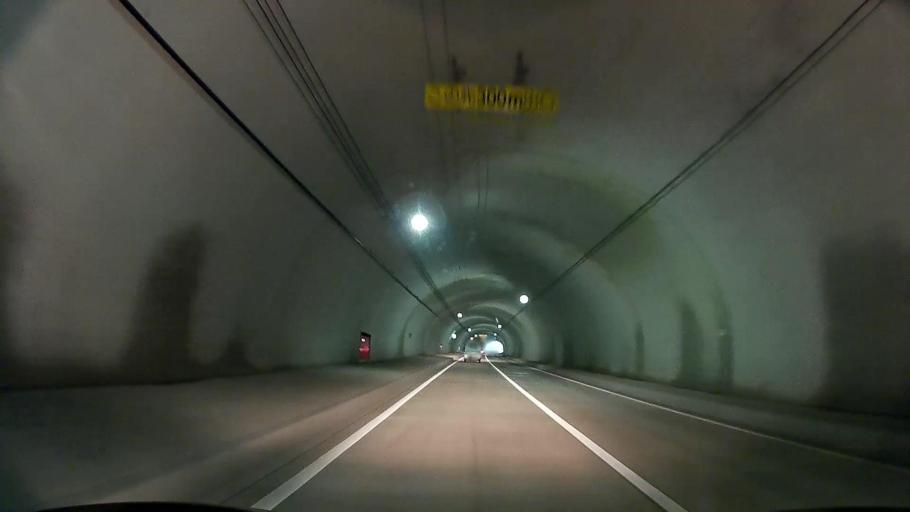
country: JP
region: Gunma
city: Nakanojomachi
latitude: 36.5304
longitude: 138.7168
